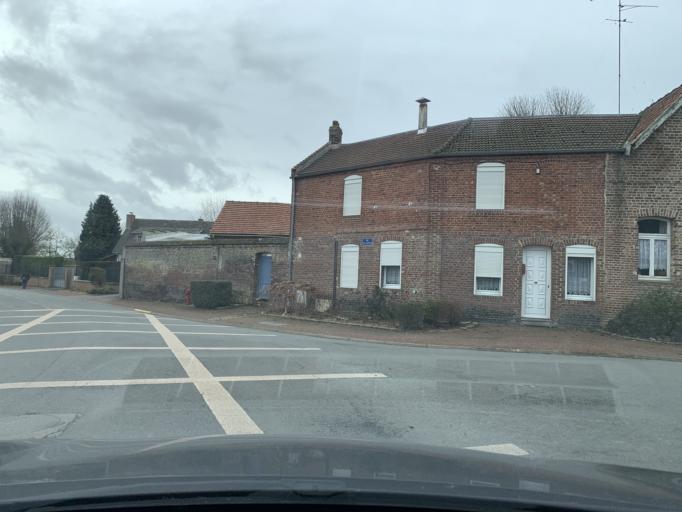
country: FR
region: Nord-Pas-de-Calais
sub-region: Departement du Nord
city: Escaudoeuvres
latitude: 50.1580
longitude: 3.2798
